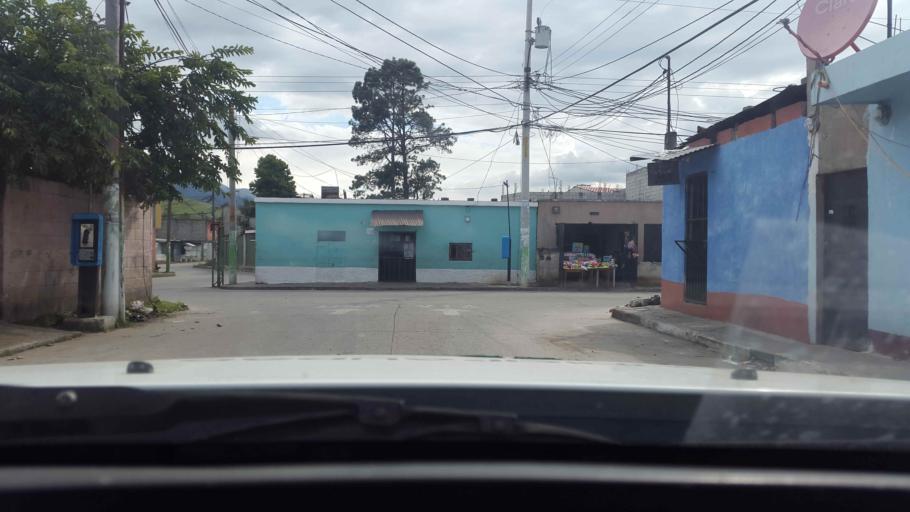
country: GT
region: Guatemala
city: Petapa
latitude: 14.5008
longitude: -90.5637
